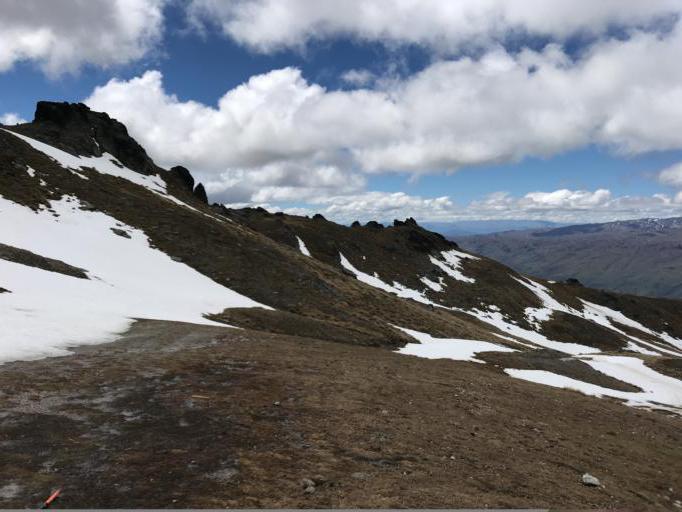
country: NZ
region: Otago
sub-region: Queenstown-Lakes District
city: Arrowtown
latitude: -44.8574
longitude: 168.9464
